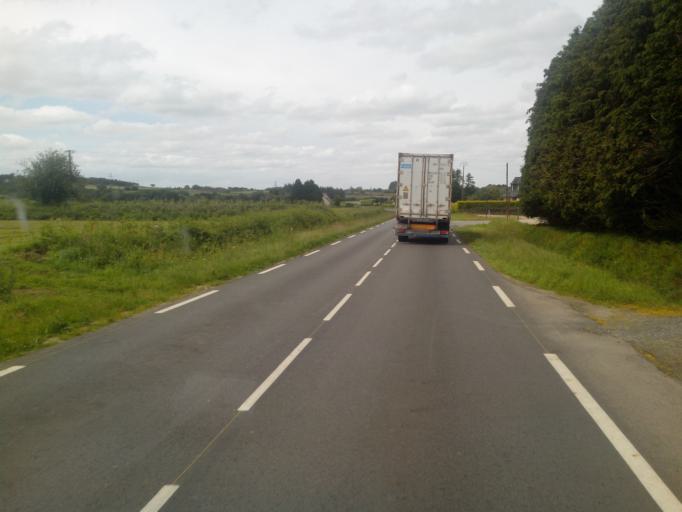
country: FR
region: Brittany
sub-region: Departement du Finistere
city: Guerlesquin
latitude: 48.5355
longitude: -3.5979
